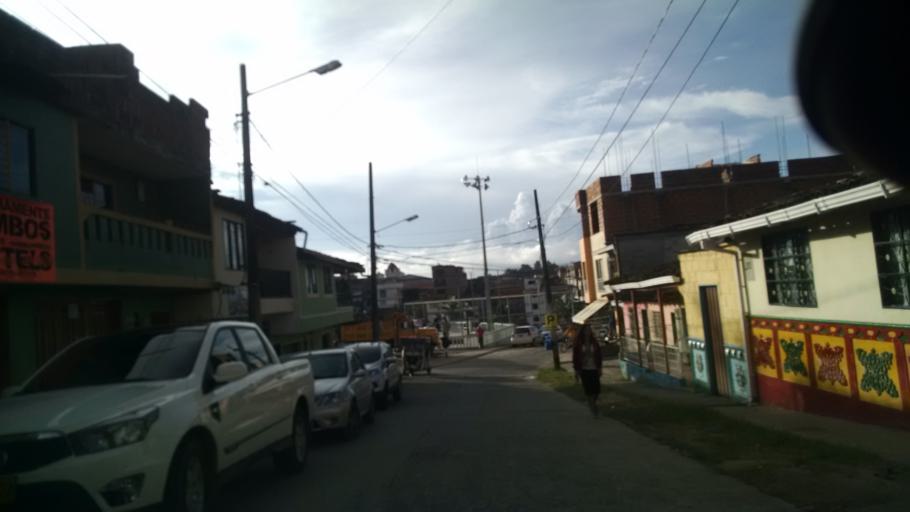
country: CO
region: Antioquia
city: Guatape
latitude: 6.2331
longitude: -75.1583
